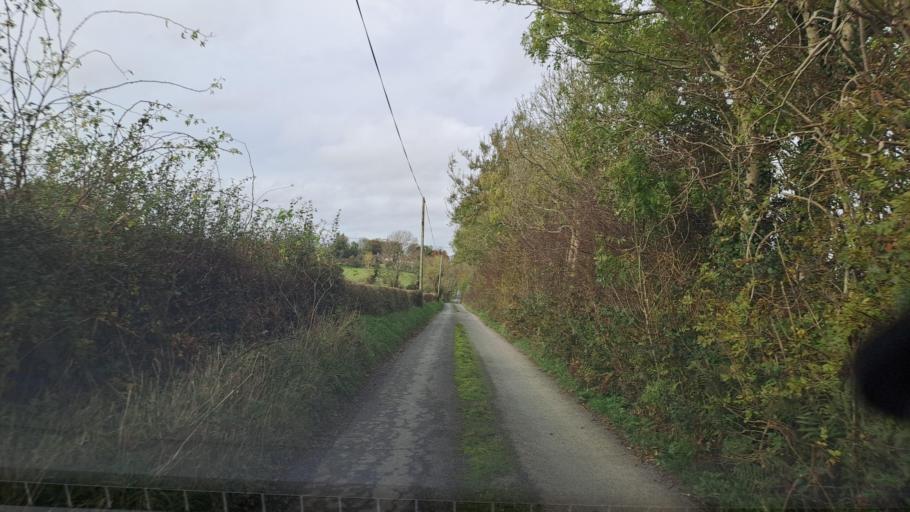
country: IE
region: Ulster
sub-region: An Cabhan
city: Kingscourt
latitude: 54.0319
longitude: -6.8465
